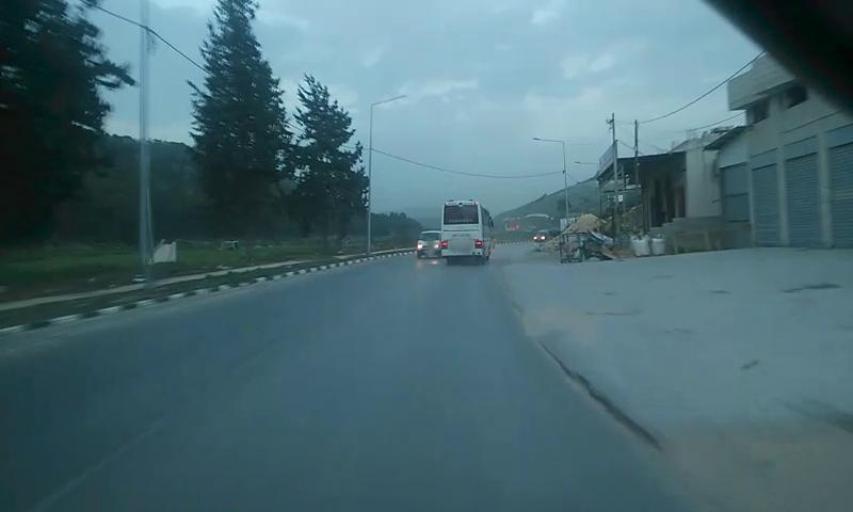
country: PS
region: West Bank
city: Iktabah
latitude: 32.3190
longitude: 35.0657
